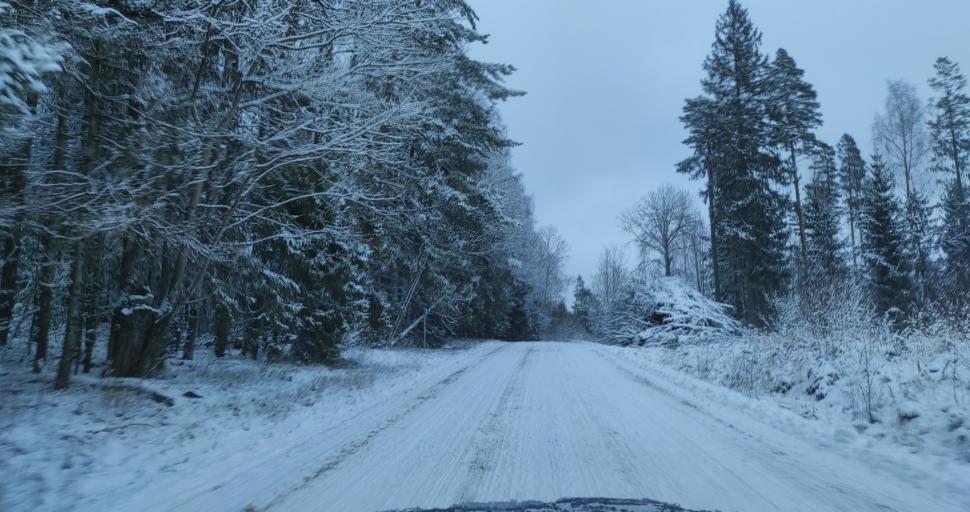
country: LV
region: Alsunga
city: Alsunga
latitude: 56.9572
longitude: 21.7178
